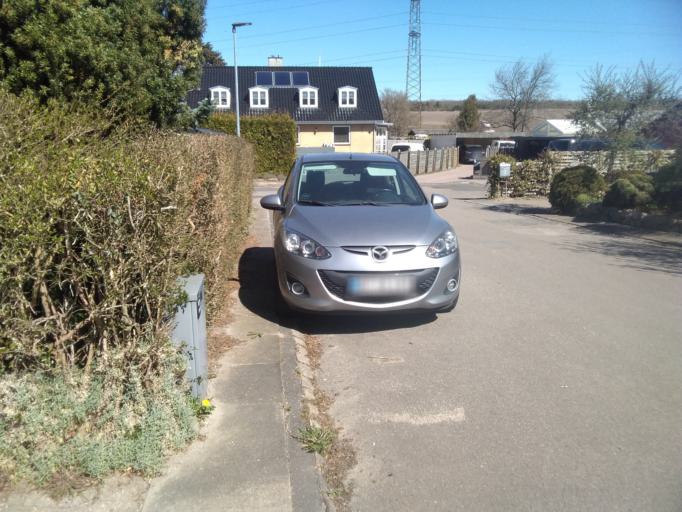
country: DK
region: Zealand
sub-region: Roskilde Kommune
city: Jyllinge
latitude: 55.7706
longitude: 12.1193
